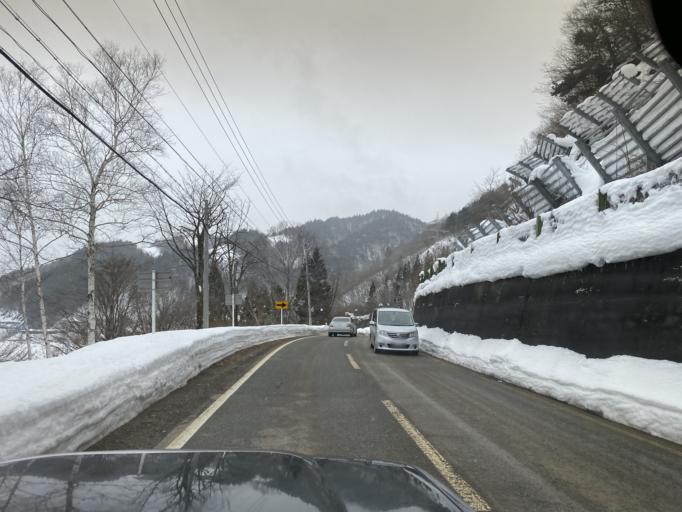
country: JP
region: Gifu
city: Takayama
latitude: 36.0958
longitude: 136.9361
